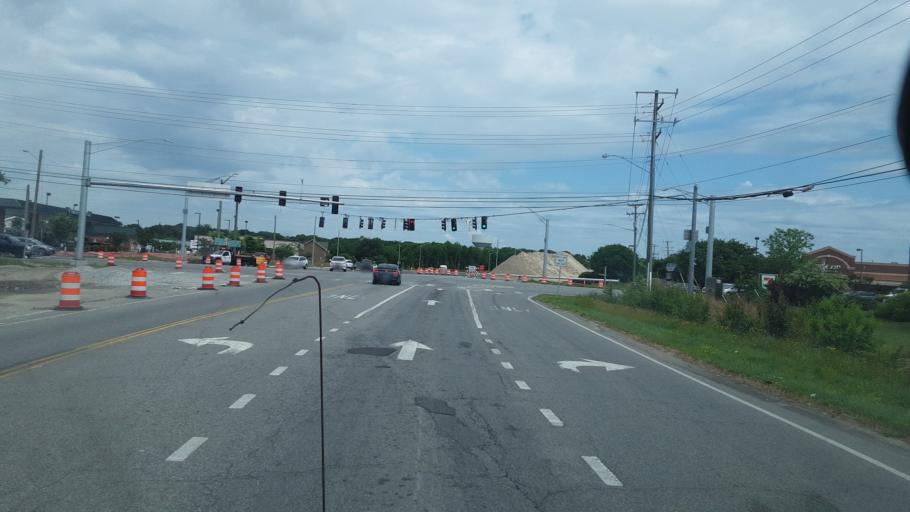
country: US
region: Virginia
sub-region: City of Virginia Beach
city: Virginia Beach
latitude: 36.7514
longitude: -76.0091
